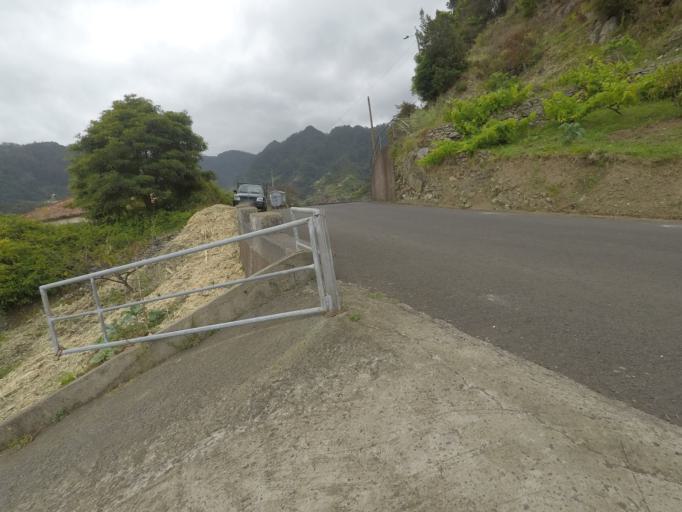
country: PT
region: Madeira
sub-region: Santana
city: Santana
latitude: 32.7657
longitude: -16.8317
